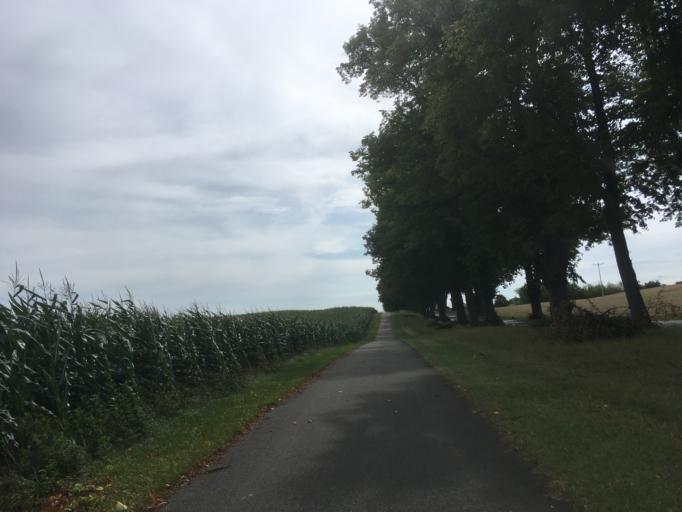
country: DE
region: Brandenburg
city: Mittenwalde
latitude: 53.2510
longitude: 13.6387
